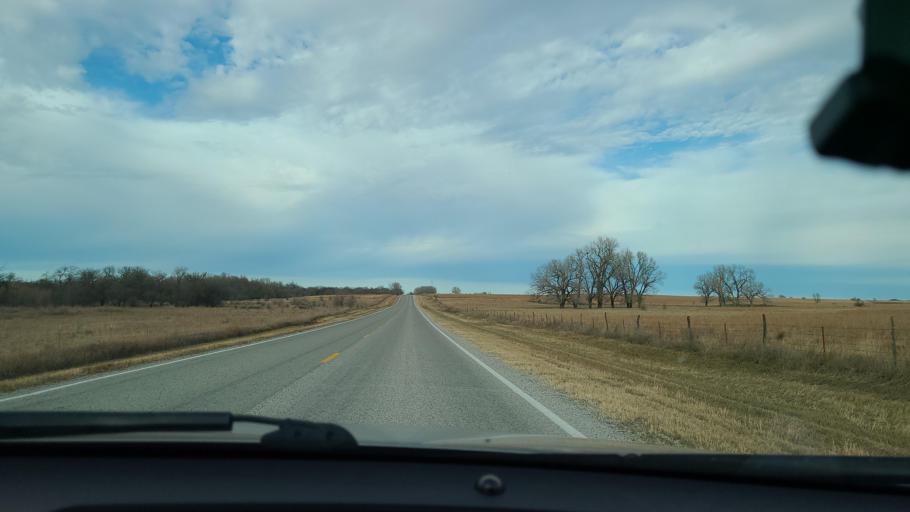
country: US
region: Kansas
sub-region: McPherson County
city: Inman
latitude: 38.3376
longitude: -97.9245
